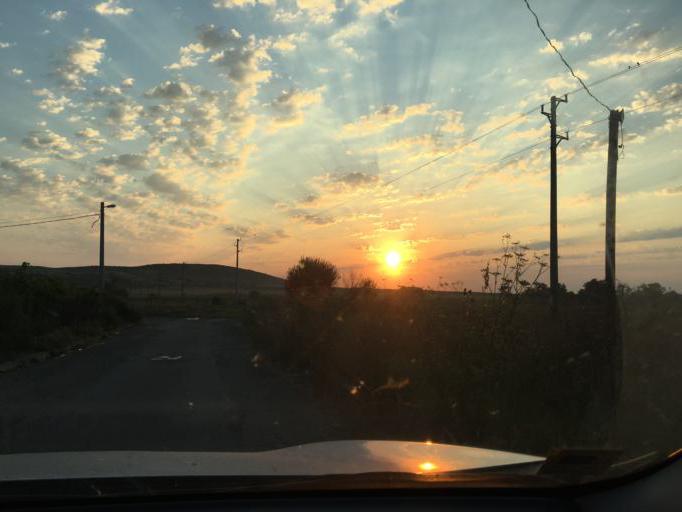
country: BG
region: Burgas
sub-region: Obshtina Burgas
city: Burgas
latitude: 42.6096
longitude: 27.4972
